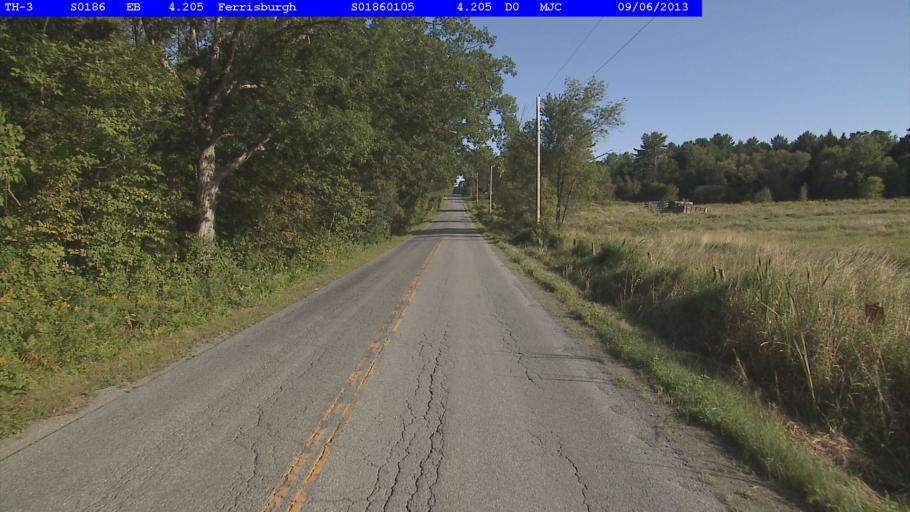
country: US
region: Vermont
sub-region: Addison County
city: Vergennes
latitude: 44.1682
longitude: -73.2990
